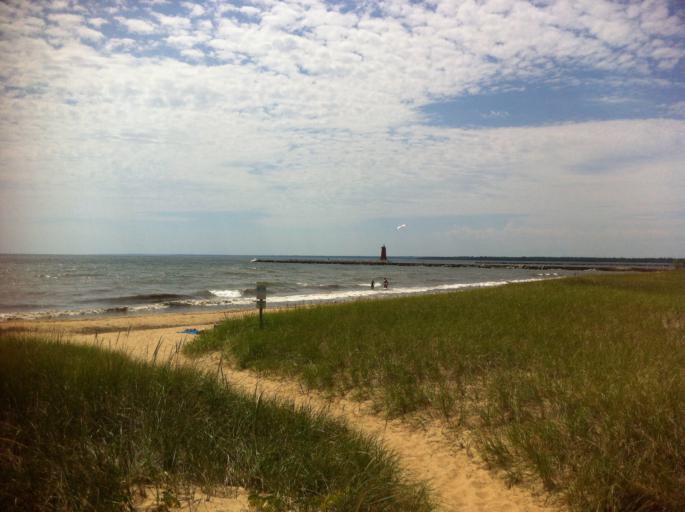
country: US
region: Michigan
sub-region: Schoolcraft County
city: Manistique
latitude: 45.9485
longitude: -86.2410
